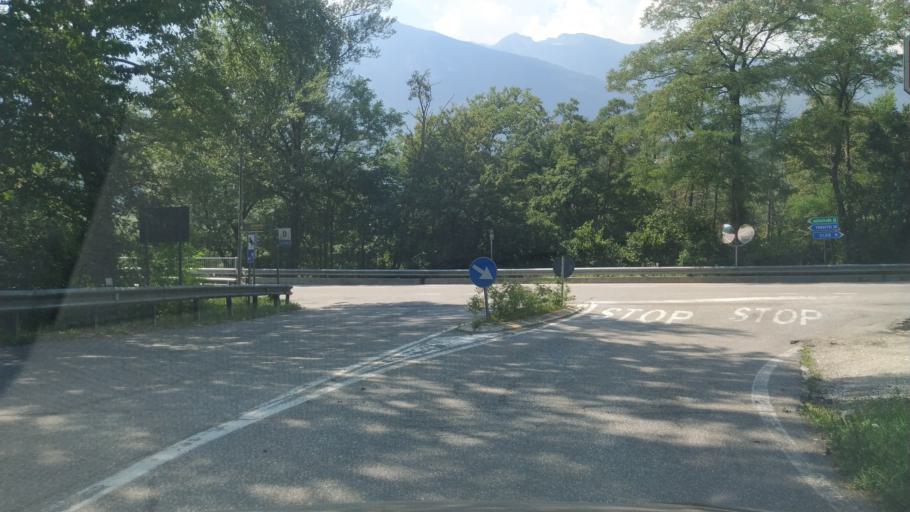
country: IT
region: Trentino-Alto Adige
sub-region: Provincia di Trento
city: Denno
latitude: 46.2479
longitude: 11.0629
